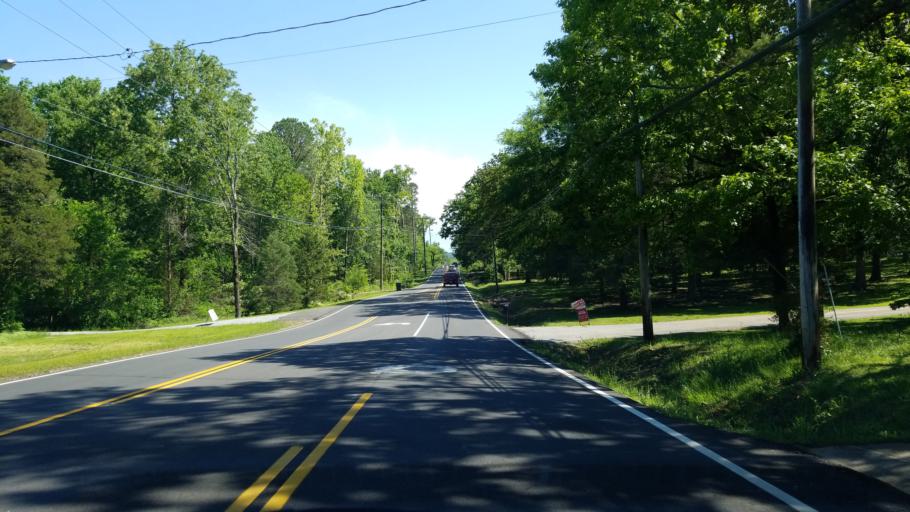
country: US
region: Tennessee
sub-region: Hamilton County
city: East Brainerd
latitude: 35.0457
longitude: -85.1471
